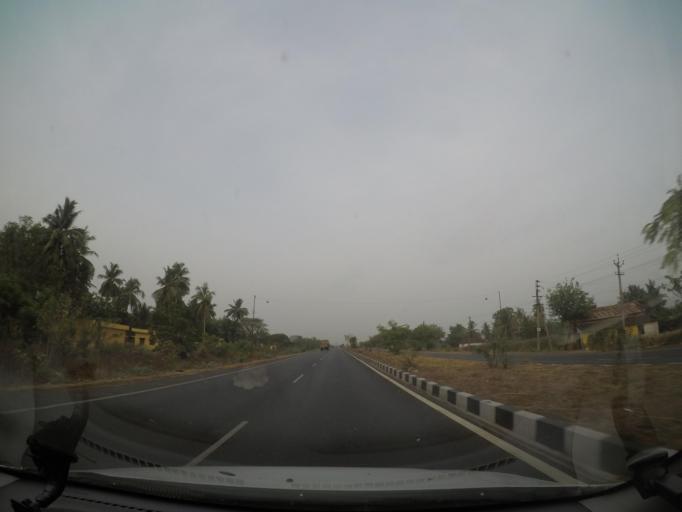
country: IN
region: Andhra Pradesh
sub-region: Krishna
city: Gannavaram
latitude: 16.6246
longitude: 80.9378
